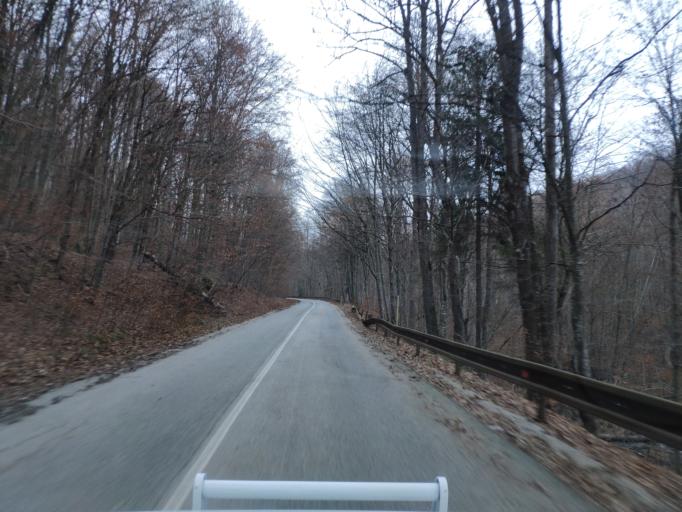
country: SK
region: Kosicky
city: Dobsina
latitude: 48.7834
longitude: 20.4759
